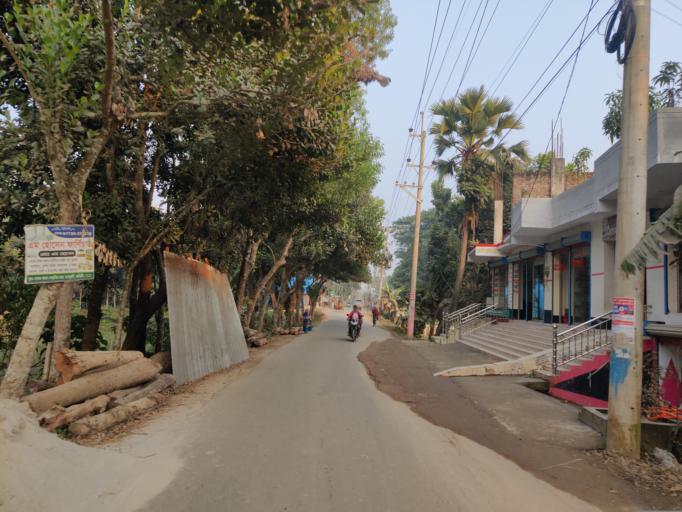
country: BD
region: Dhaka
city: Bajitpur
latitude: 24.1586
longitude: 90.7539
